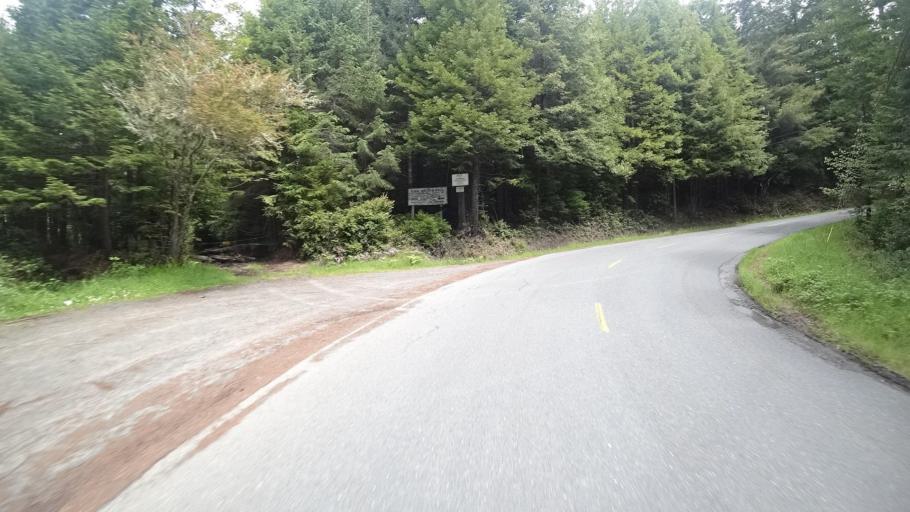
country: US
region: California
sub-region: Humboldt County
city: Bayside
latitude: 40.7874
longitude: -124.0730
